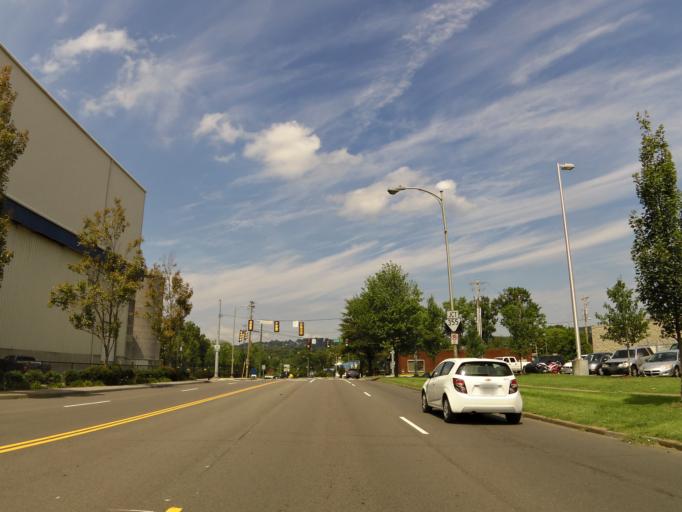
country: US
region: Tennessee
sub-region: Sullivan County
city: Kingsport
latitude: 36.5514
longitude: -82.5666
